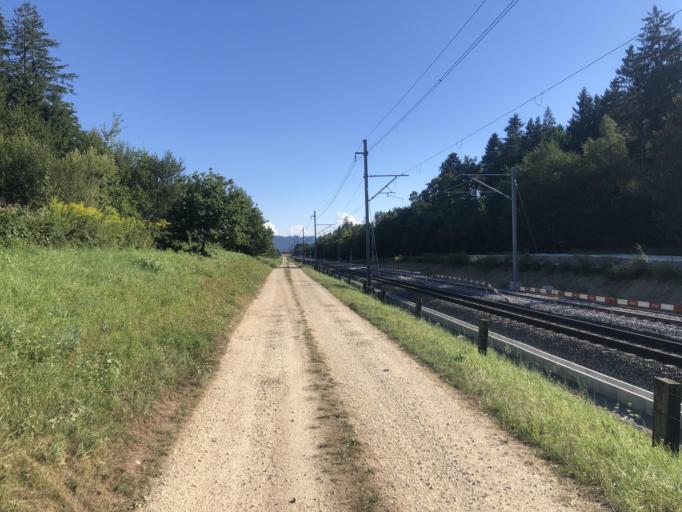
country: CH
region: Bern
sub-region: Bern-Mittelland District
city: Jegenstorf
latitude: 47.0697
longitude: 7.5073
